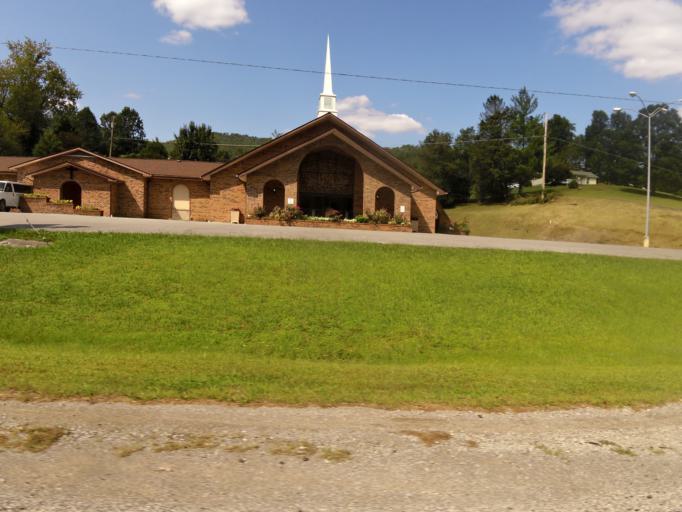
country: US
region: Kentucky
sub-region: Harlan County
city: Loyall
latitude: 36.8116
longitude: -83.4965
